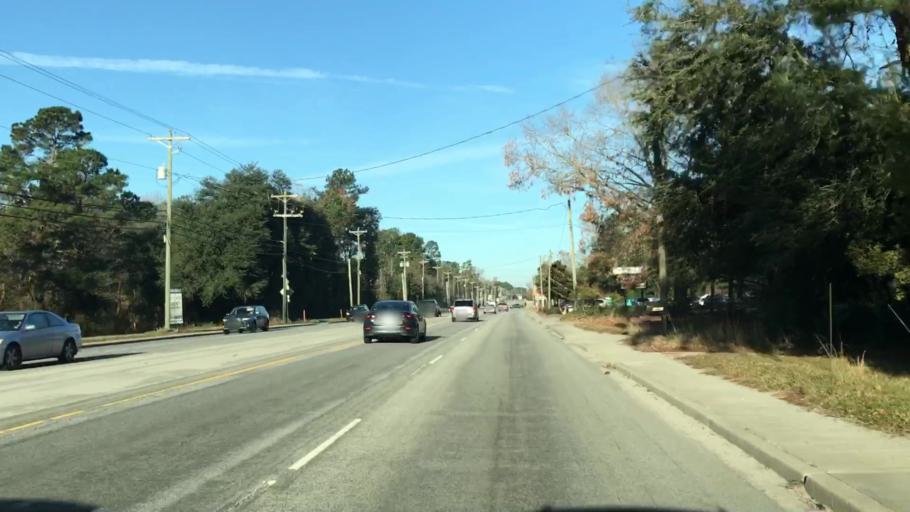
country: US
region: South Carolina
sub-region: Berkeley County
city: Ladson
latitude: 32.9833
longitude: -80.0903
